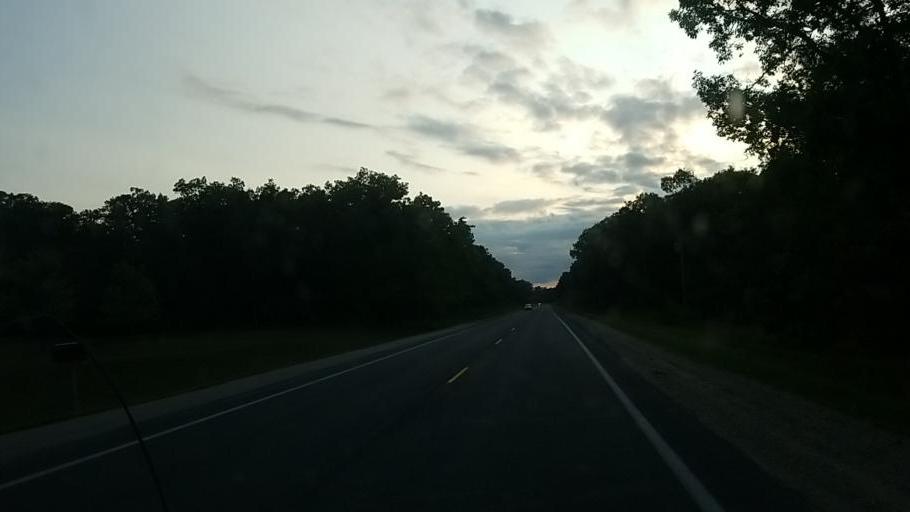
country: US
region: Michigan
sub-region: Newaygo County
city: Newaygo
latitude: 43.4049
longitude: -85.7636
